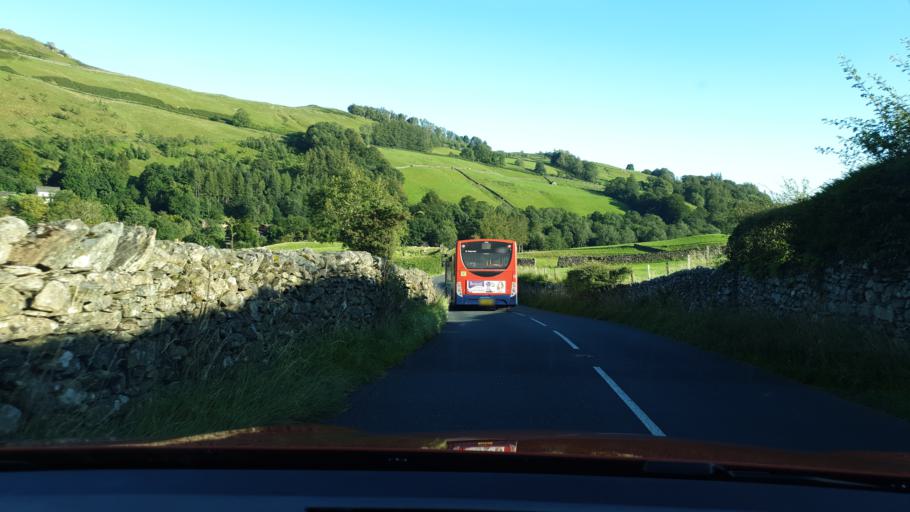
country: GB
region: England
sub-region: Cumbria
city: Windermere
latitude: 54.4223
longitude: -2.9057
